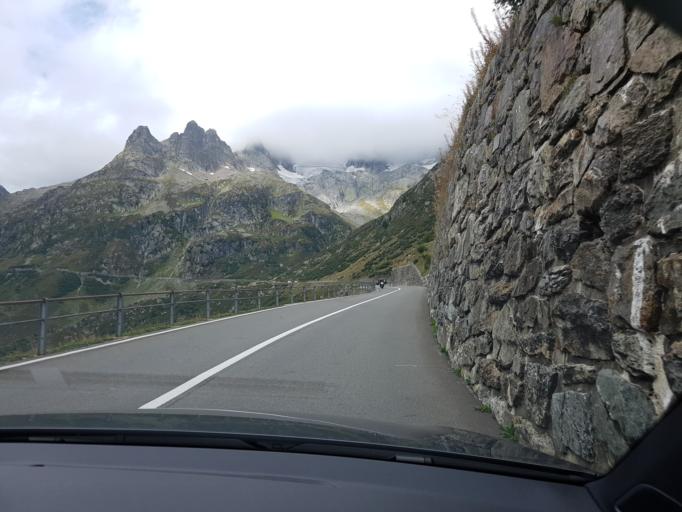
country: CH
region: Obwalden
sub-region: Obwalden
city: Engelberg
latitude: 46.7463
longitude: 8.4800
